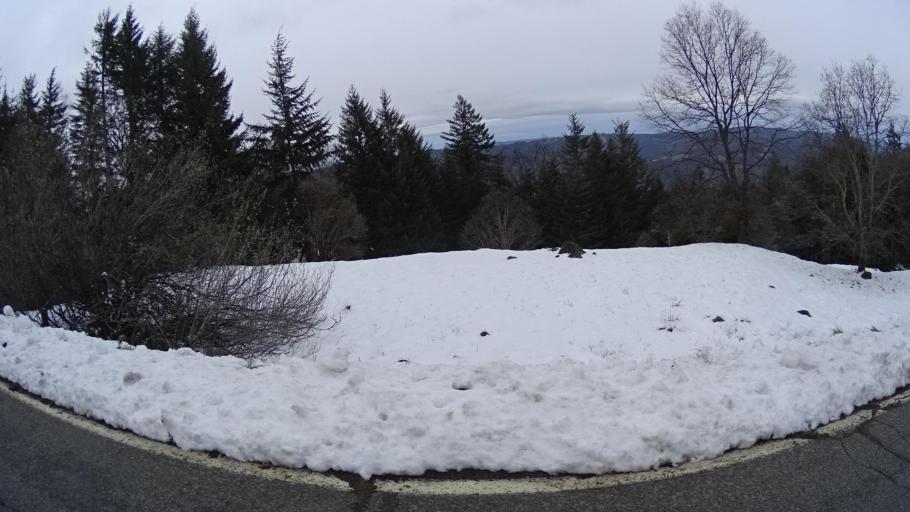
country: US
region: California
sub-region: Humboldt County
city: Willow Creek
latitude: 40.8724
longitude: -123.7533
